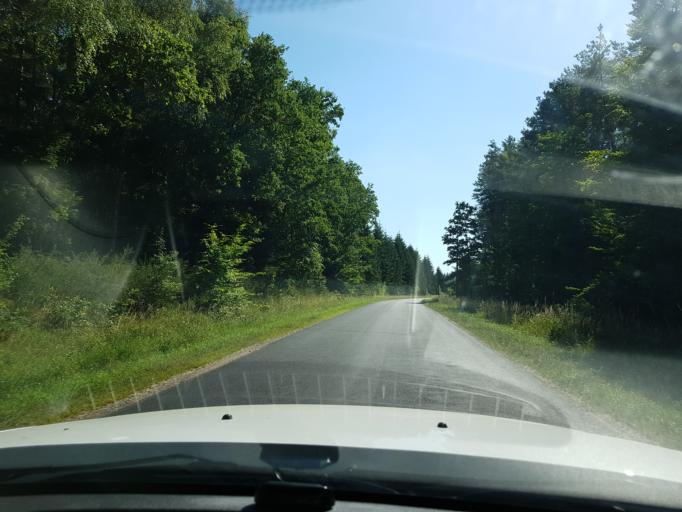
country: PL
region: West Pomeranian Voivodeship
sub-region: Powiat swidwinski
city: Slawoborze
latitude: 53.9039
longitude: 15.7421
